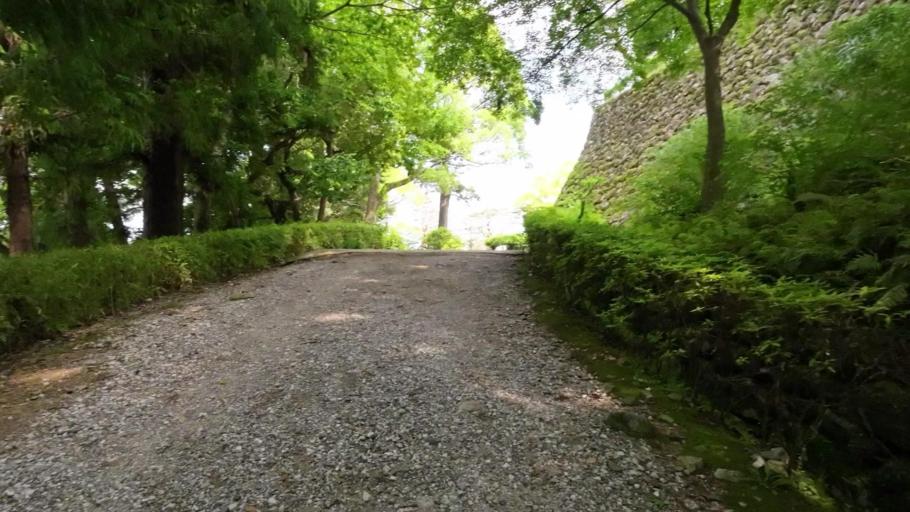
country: JP
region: Kochi
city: Kochi-shi
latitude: 33.5622
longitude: 133.5319
